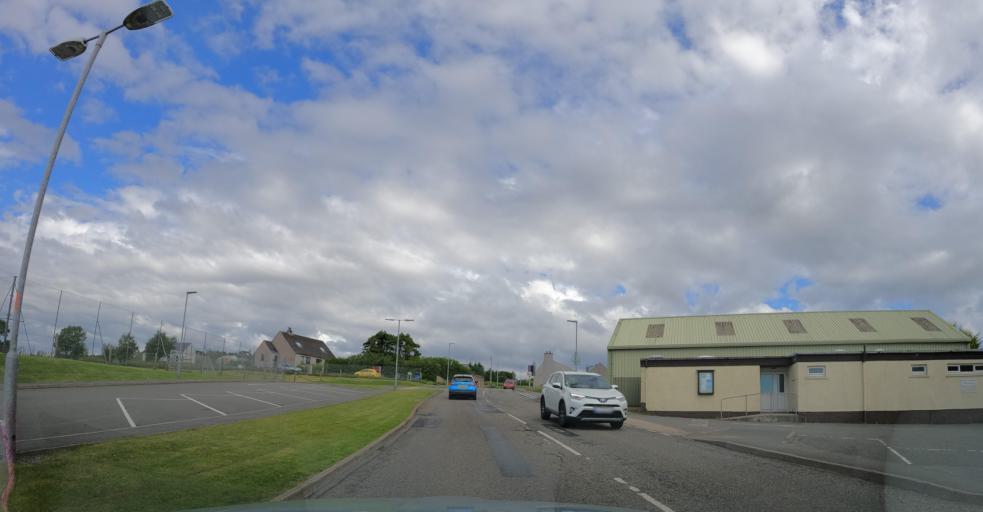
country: GB
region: Scotland
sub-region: Eilean Siar
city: Isle of Lewis
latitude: 58.2301
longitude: -6.3896
